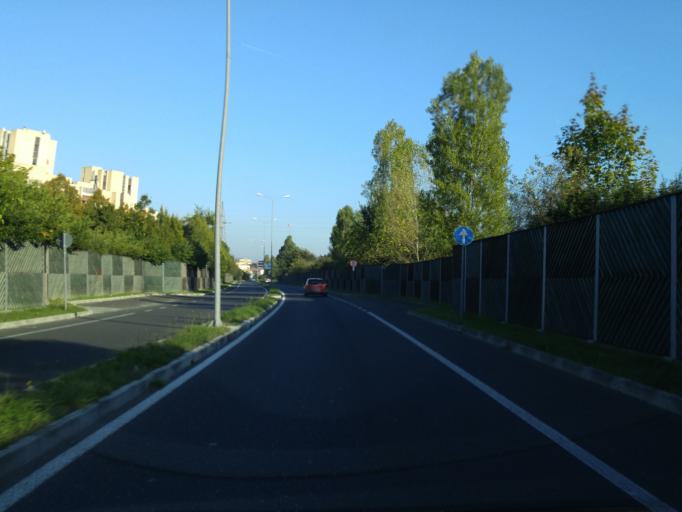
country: IT
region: The Marches
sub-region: Provincia di Pesaro e Urbino
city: Pesaro
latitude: 43.8895
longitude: 12.8954
